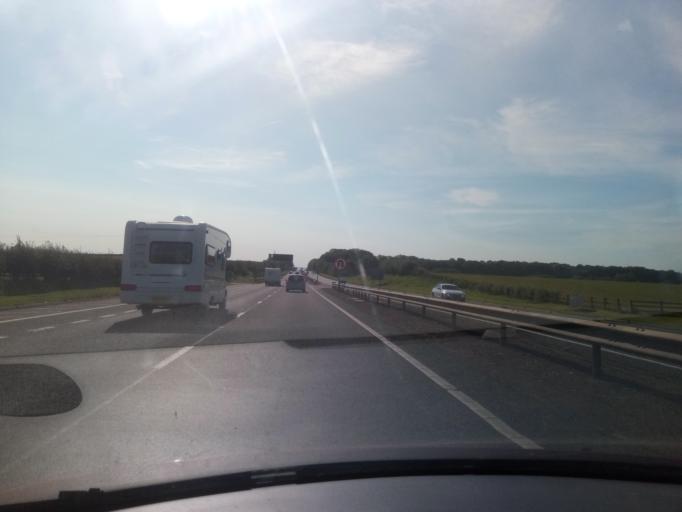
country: GB
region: England
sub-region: Hartlepool
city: Elwick
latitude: 54.6522
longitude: -1.3025
